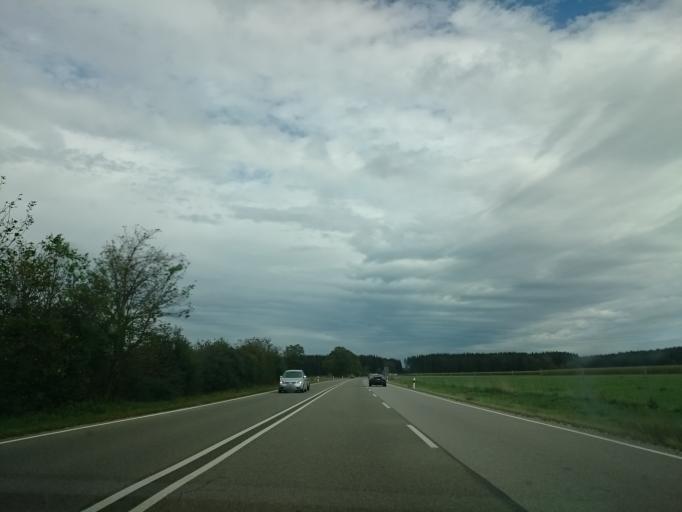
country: DE
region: Bavaria
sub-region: Swabia
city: Jengen
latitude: 47.9751
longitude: 10.6894
